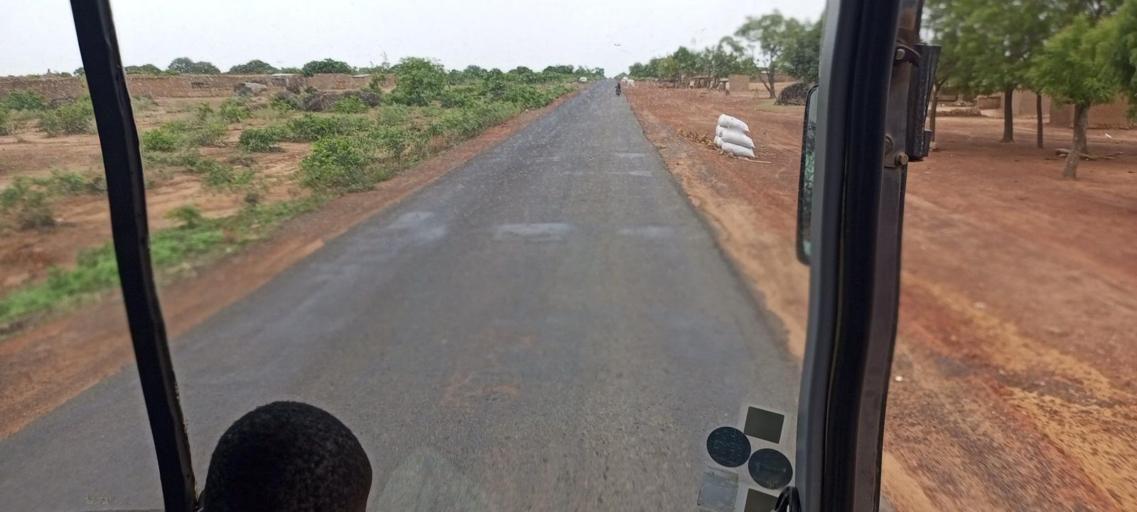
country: ML
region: Sikasso
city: Koutiala
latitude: 12.5366
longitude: -5.5718
